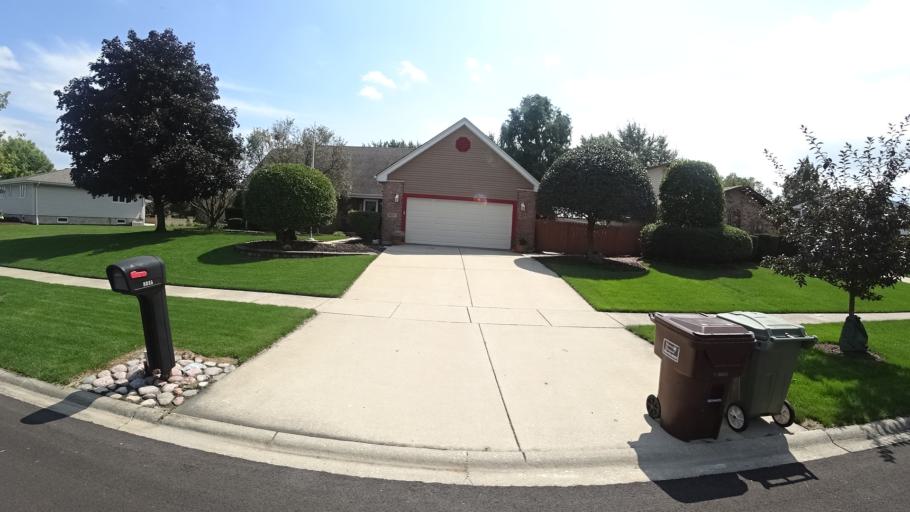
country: US
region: Illinois
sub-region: Cook County
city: Tinley Park
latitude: 41.5720
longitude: -87.8146
